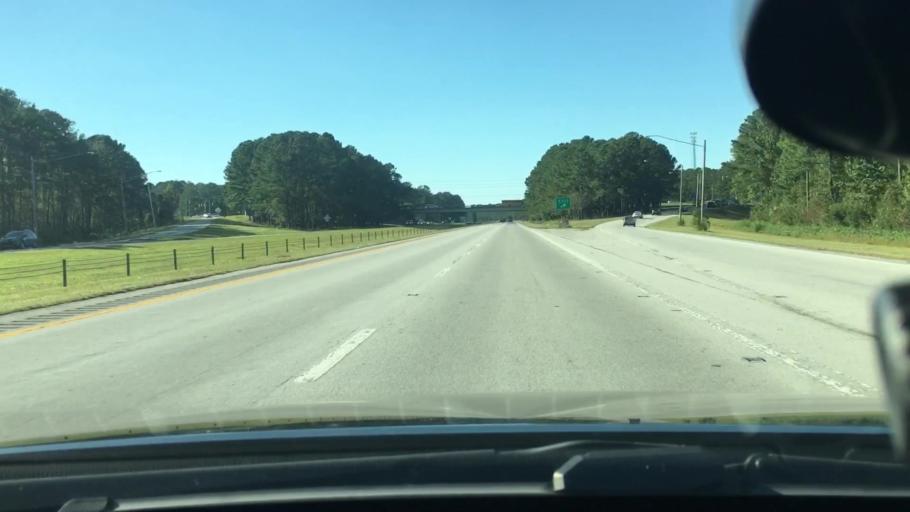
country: US
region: North Carolina
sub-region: Craven County
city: Trent Woods
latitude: 35.1104
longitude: -77.0939
